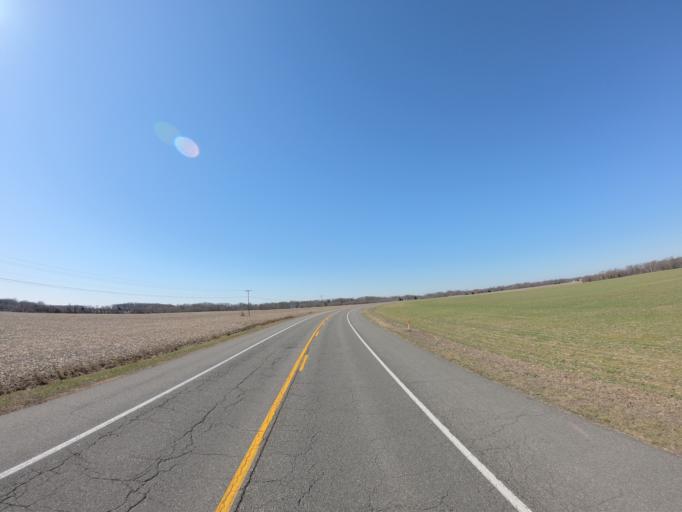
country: US
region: Delaware
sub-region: New Castle County
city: Townsend
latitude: 39.3438
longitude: -75.8466
